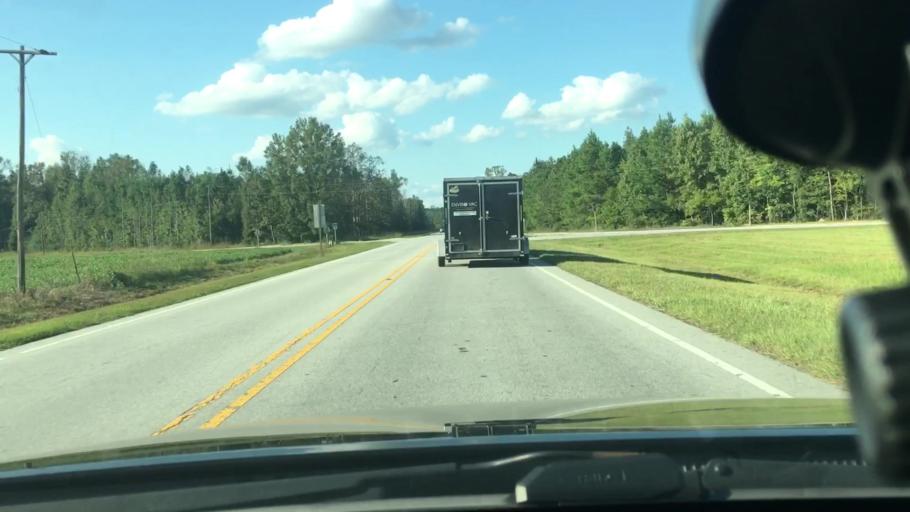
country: US
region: North Carolina
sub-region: Craven County
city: Vanceboro
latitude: 35.2943
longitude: -77.1303
